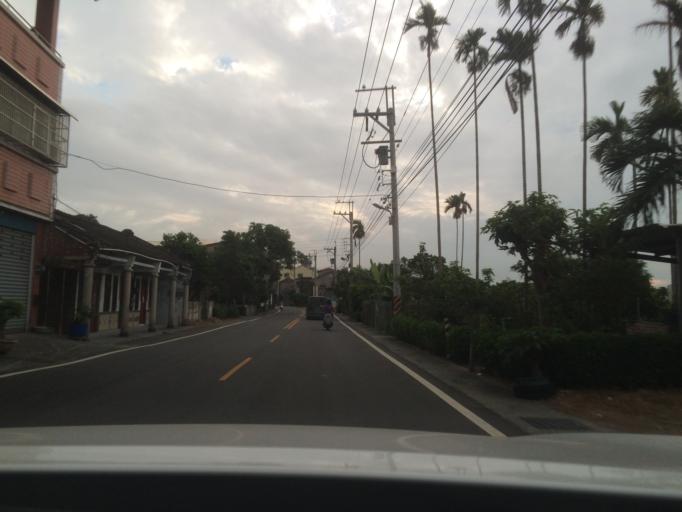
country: TW
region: Taiwan
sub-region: Nantou
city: Nantou
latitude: 23.8662
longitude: 120.6030
